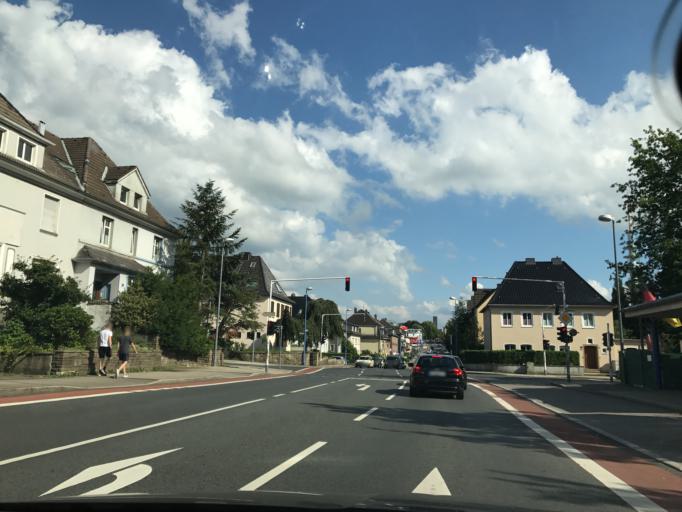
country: DE
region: North Rhine-Westphalia
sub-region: Regierungsbezirk Dusseldorf
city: Velbert
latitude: 51.3373
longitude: 7.0451
